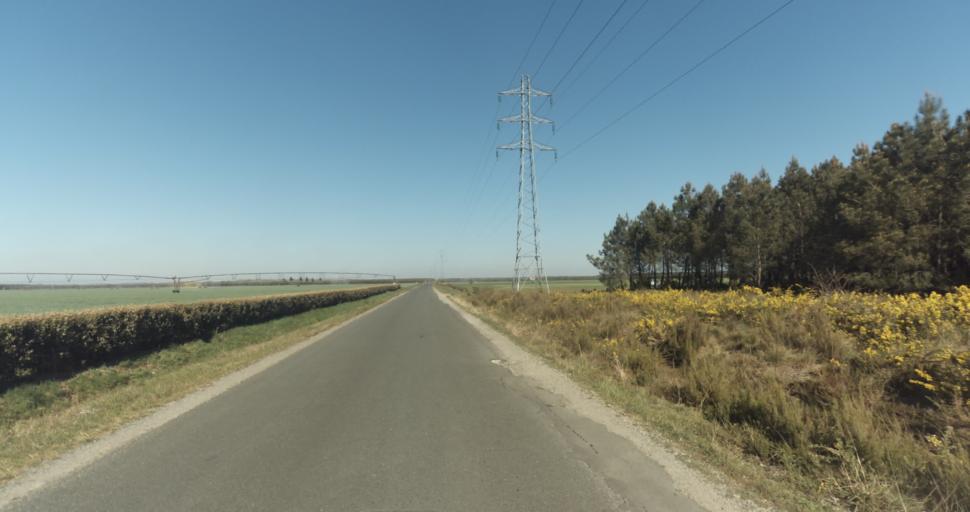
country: FR
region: Aquitaine
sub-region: Departement de la Gironde
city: Marcheprime
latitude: 44.7444
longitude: -0.8317
